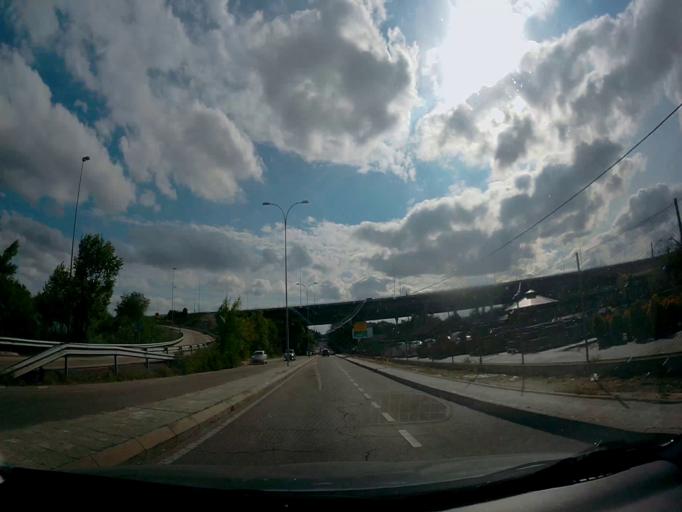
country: ES
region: Madrid
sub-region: Provincia de Madrid
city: Mostoles
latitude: 40.3372
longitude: -3.8478
